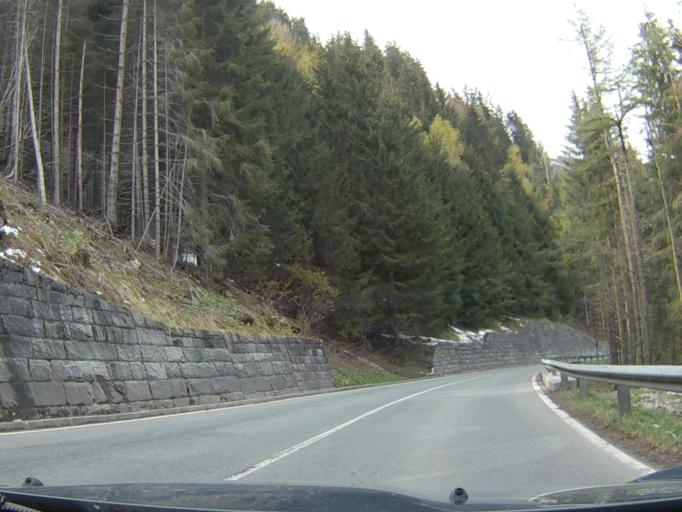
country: AT
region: Salzburg
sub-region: Politischer Bezirk Zell am See
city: Krimml
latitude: 47.2127
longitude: 12.1649
